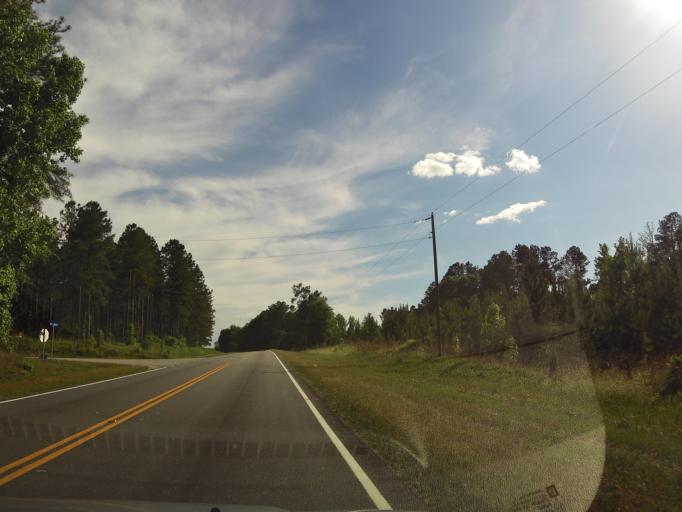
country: US
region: South Carolina
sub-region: Allendale County
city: Fairfax
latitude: 33.0112
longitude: -81.2168
